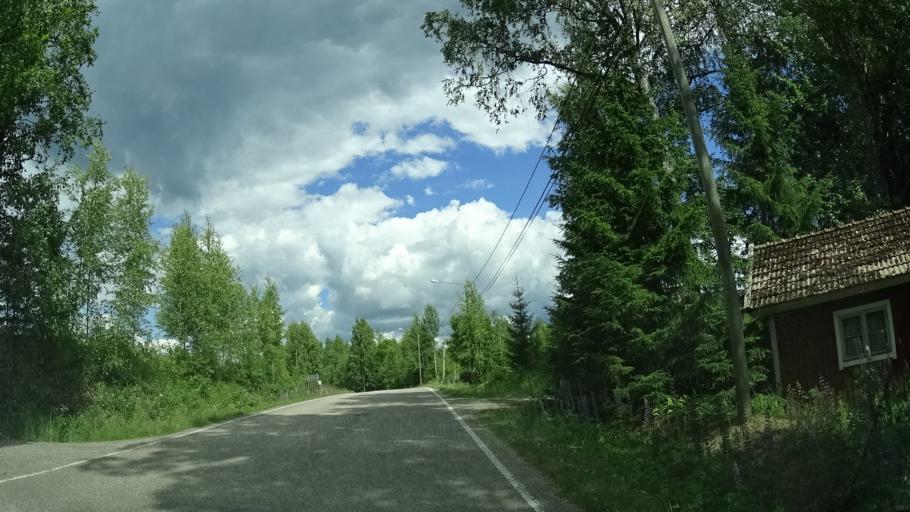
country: FI
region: Uusimaa
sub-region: Helsinki
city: Vihti
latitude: 60.4357
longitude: 24.5223
